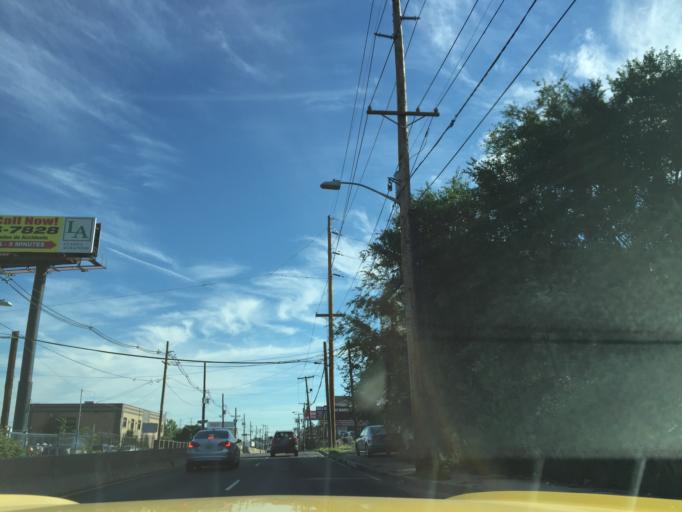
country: US
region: New Jersey
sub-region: Hudson County
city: Hoboken
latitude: 40.7621
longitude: -74.0496
